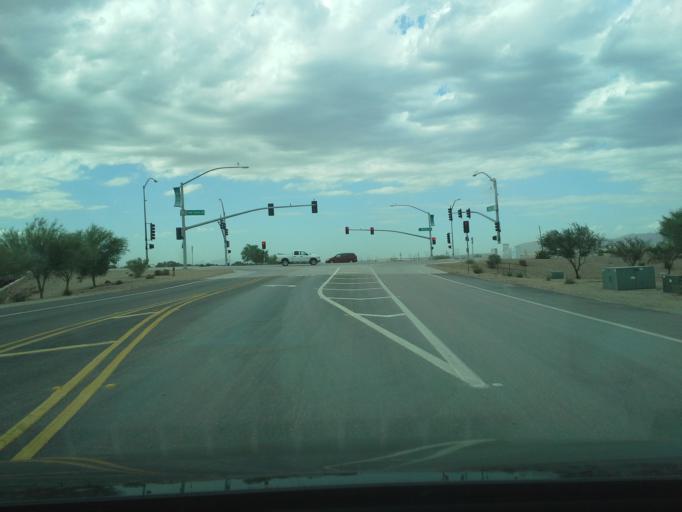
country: US
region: Arizona
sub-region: Pima County
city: Tortolita
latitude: 32.3763
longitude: -111.1122
